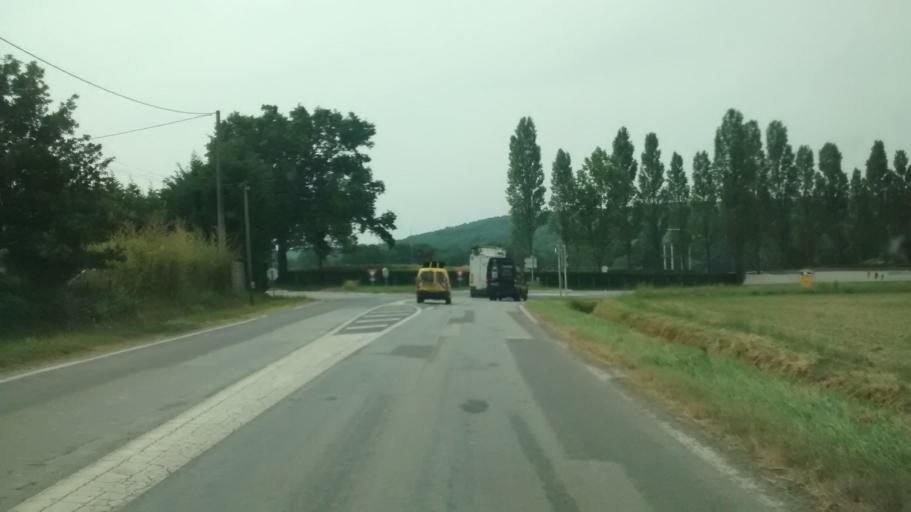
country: FR
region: Brittany
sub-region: Departement du Morbihan
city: Guer
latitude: 47.9042
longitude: -2.1332
